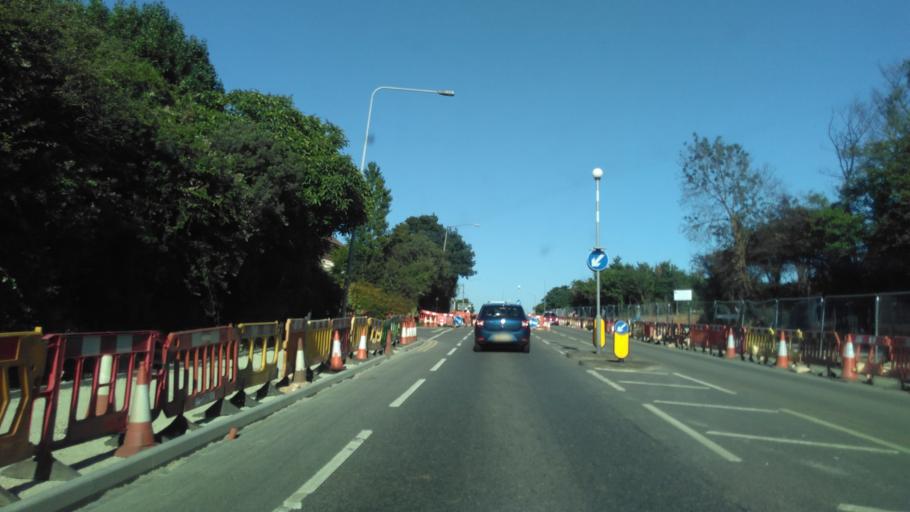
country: GB
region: England
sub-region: Kent
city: Whitstable
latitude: 51.3420
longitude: 1.0153
